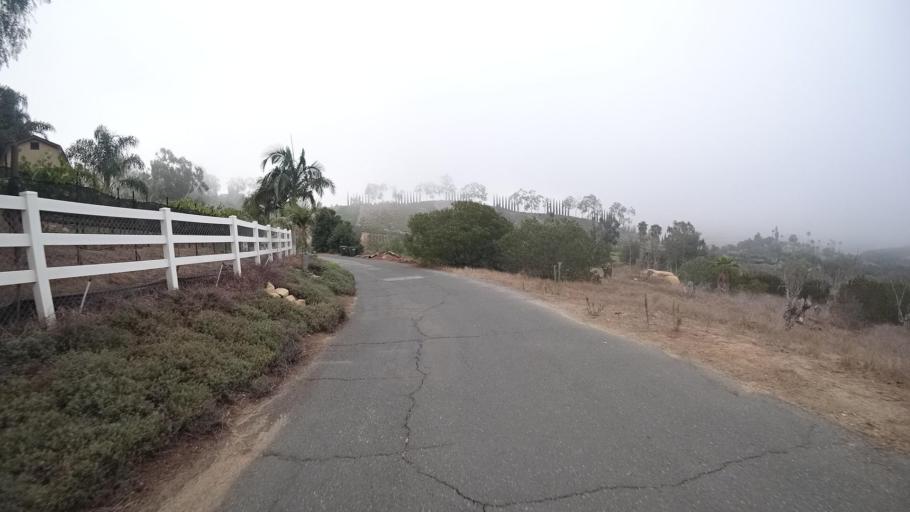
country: US
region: California
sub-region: San Diego County
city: Bonsall
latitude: 33.3281
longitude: -117.1730
